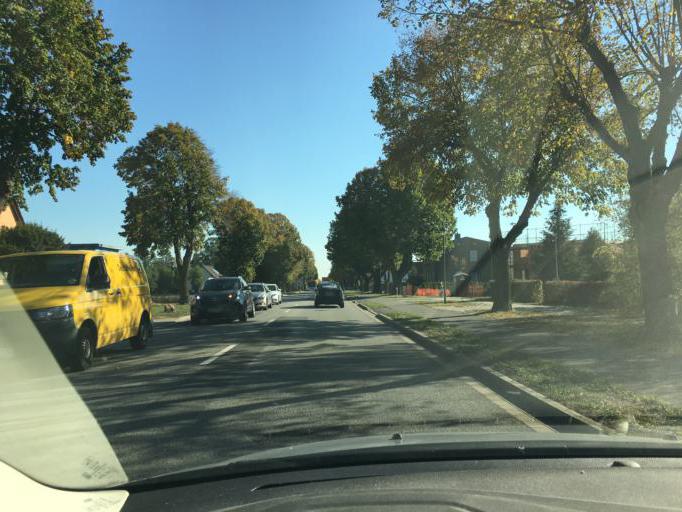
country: DE
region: Saxony-Anhalt
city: Forderstedt
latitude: 51.9038
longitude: 11.6272
